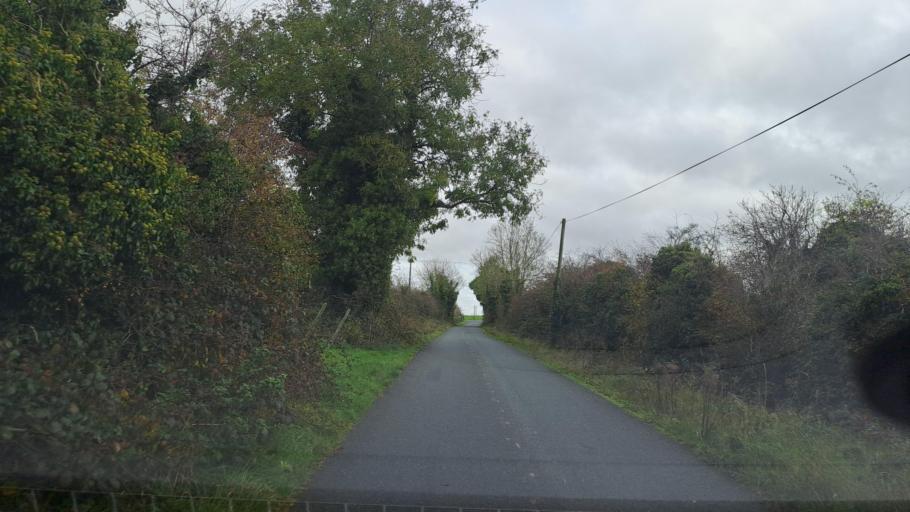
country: IE
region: Ulster
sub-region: An Cabhan
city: Bailieborough
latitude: 54.0130
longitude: -6.8918
